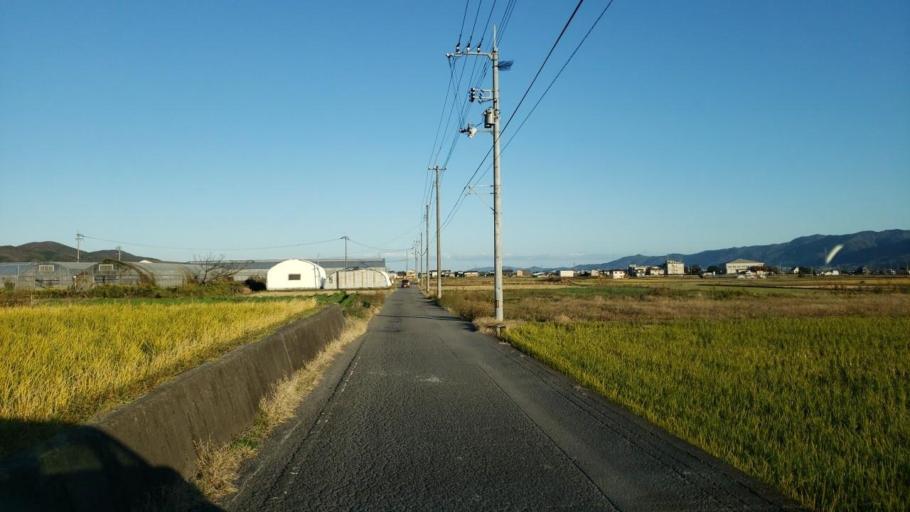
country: JP
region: Tokushima
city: Kamojimacho-jogejima
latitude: 34.0908
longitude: 134.2558
